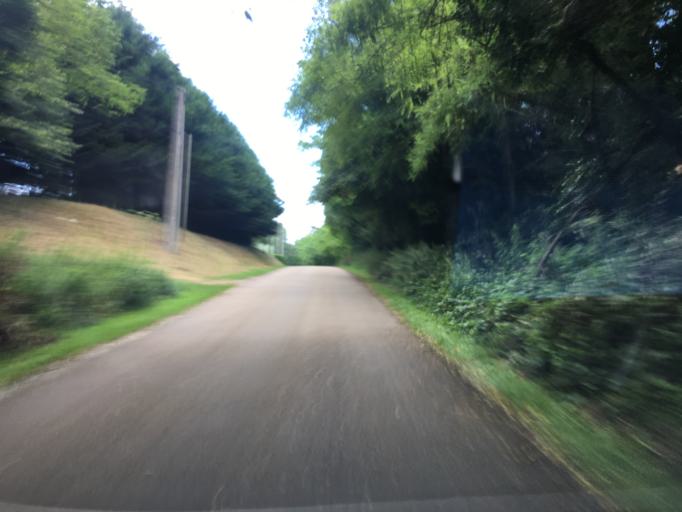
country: FR
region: Bourgogne
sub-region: Departement de l'Yonne
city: Fleury-la-Vallee
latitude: 47.8689
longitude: 3.4814
